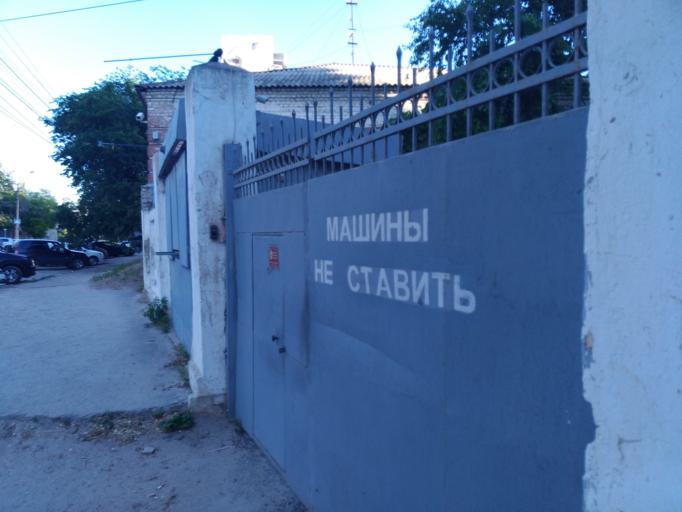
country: RU
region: Volgograd
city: Volgograd
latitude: 48.7119
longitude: 44.5040
